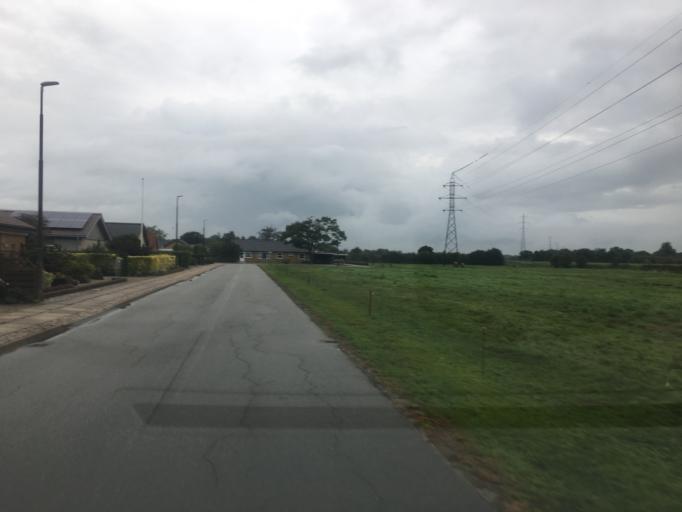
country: DK
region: South Denmark
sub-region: Tonder Kommune
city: Tonder
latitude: 54.9427
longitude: 8.8844
